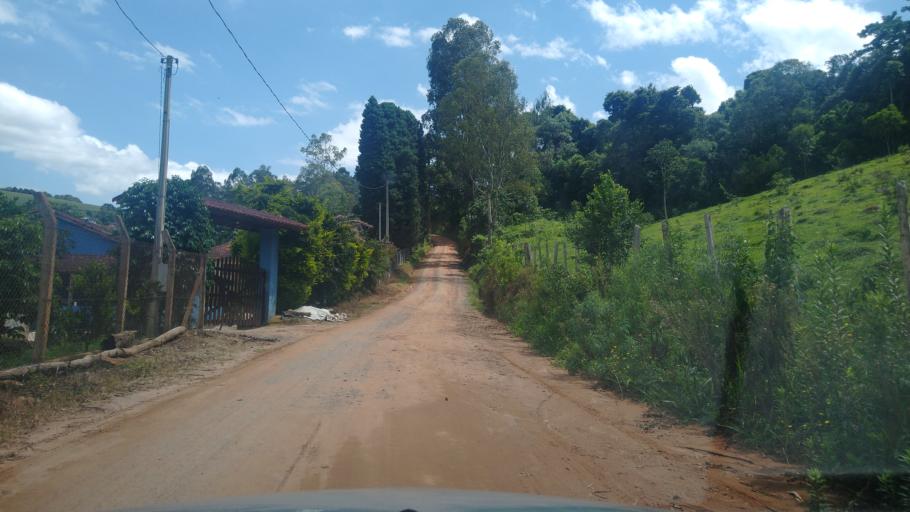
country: BR
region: Minas Gerais
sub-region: Extrema
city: Extrema
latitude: -22.7402
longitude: -46.2957
